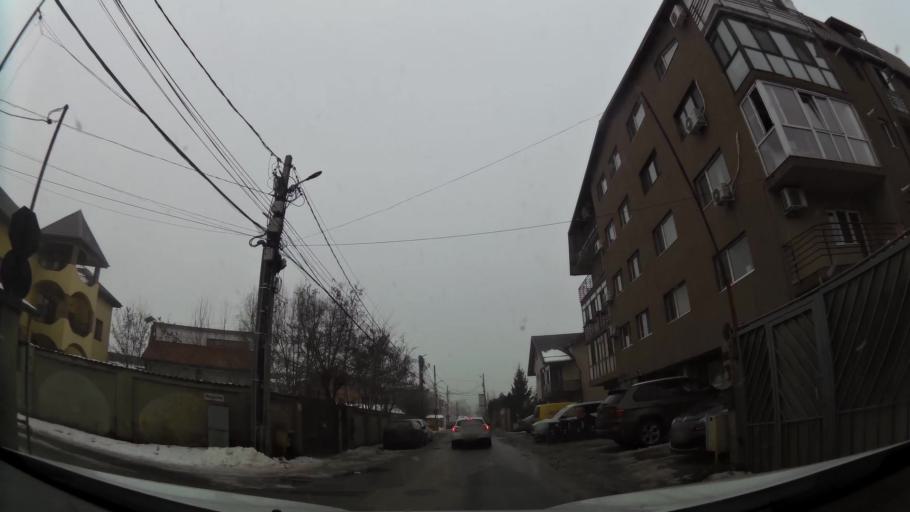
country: RO
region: Ilfov
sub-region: Comuna Chiajna
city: Rosu
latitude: 44.4517
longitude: 25.9937
